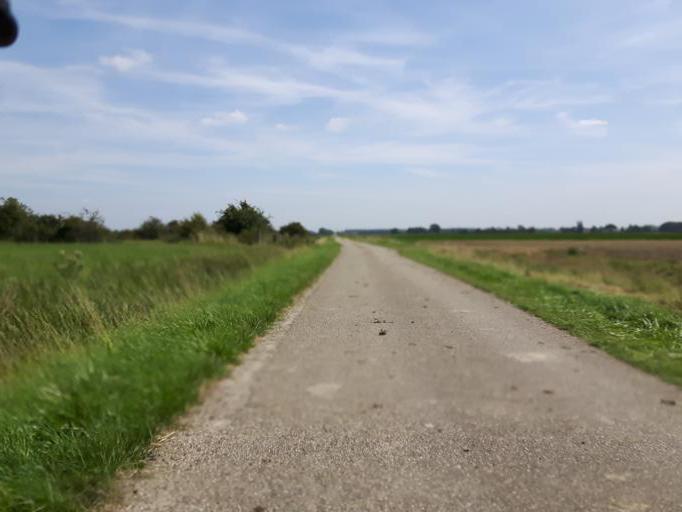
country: NL
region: Zeeland
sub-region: Gemeente Goes
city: Goes
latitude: 51.4693
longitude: 3.8422
